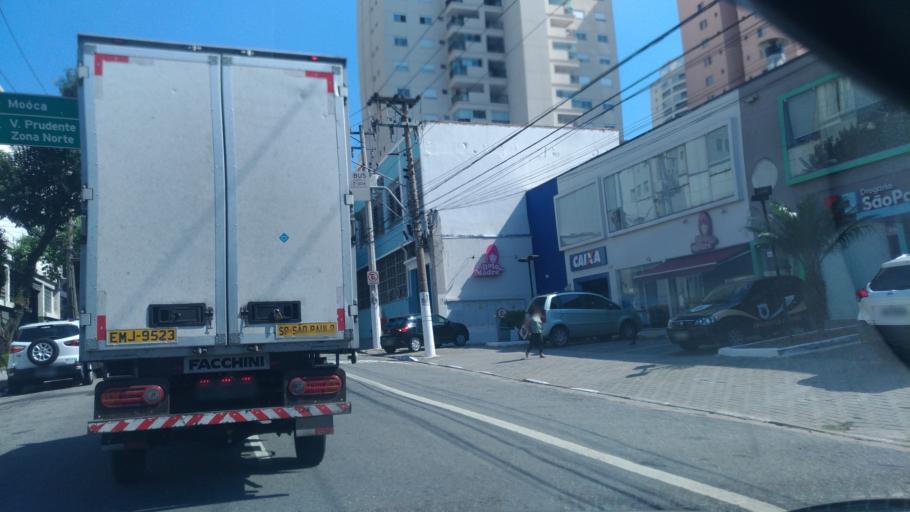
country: BR
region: Sao Paulo
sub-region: Sao Paulo
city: Sao Paulo
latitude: -23.5835
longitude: -46.6045
